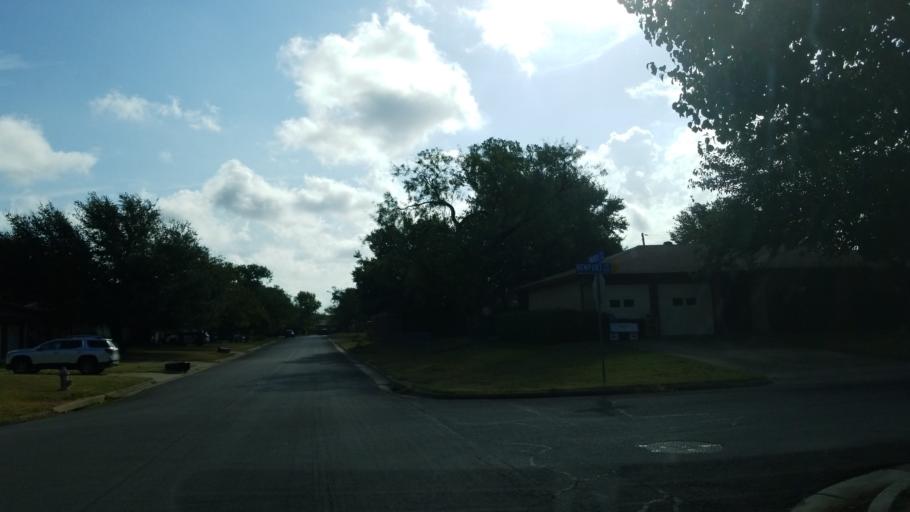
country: US
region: Texas
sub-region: Tarrant County
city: Euless
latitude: 32.8414
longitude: -97.0787
